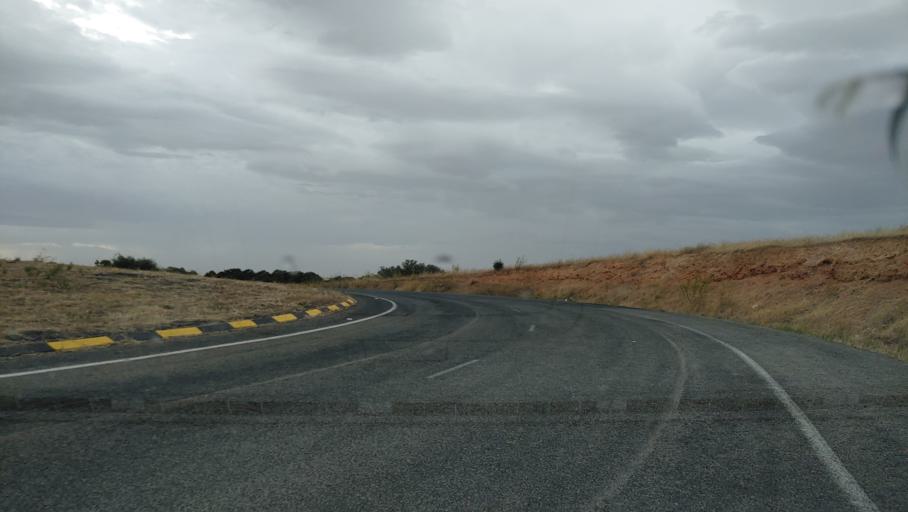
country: ES
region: Castille-La Mancha
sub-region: Provincia de Ciudad Real
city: Canada de Calatrava
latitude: 38.8754
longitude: -4.0111
